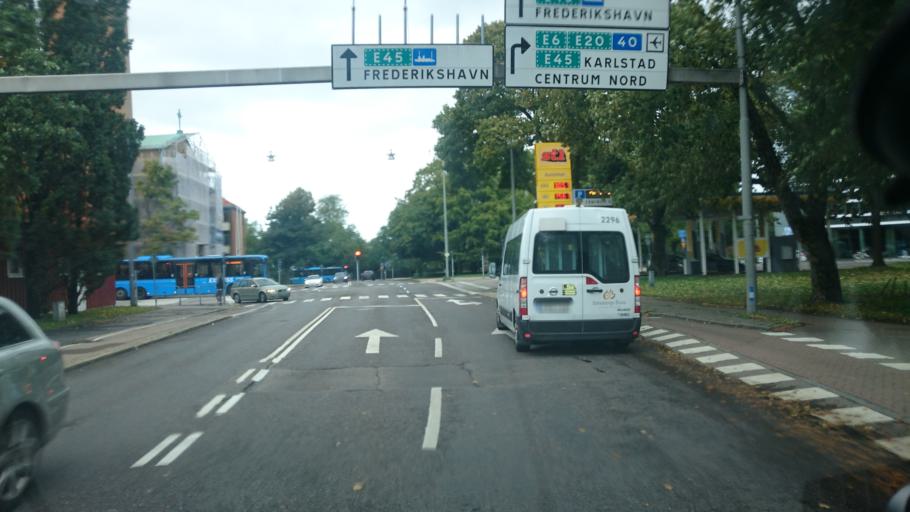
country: SE
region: Vaestra Goetaland
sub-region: Goteborg
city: Goeteborg
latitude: 57.7038
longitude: 11.9793
